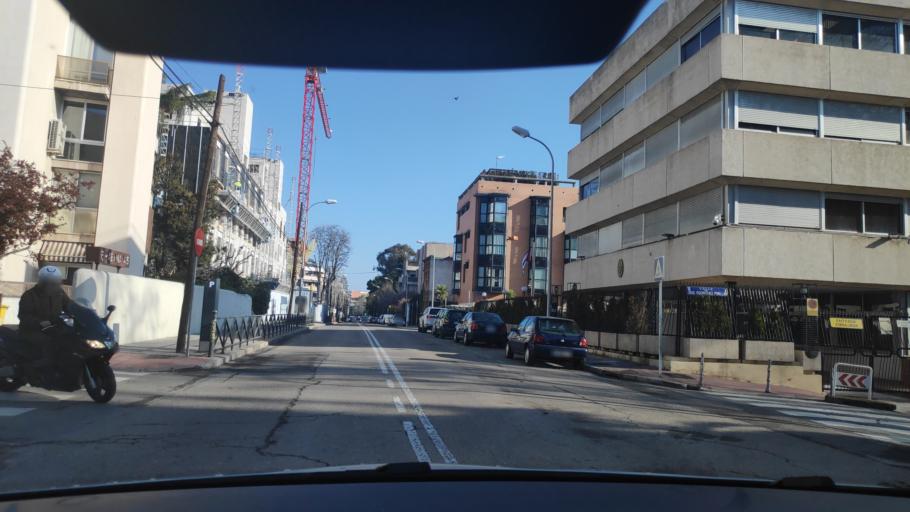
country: ES
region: Madrid
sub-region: Provincia de Madrid
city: Chamartin
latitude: 40.4617
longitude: -3.6805
